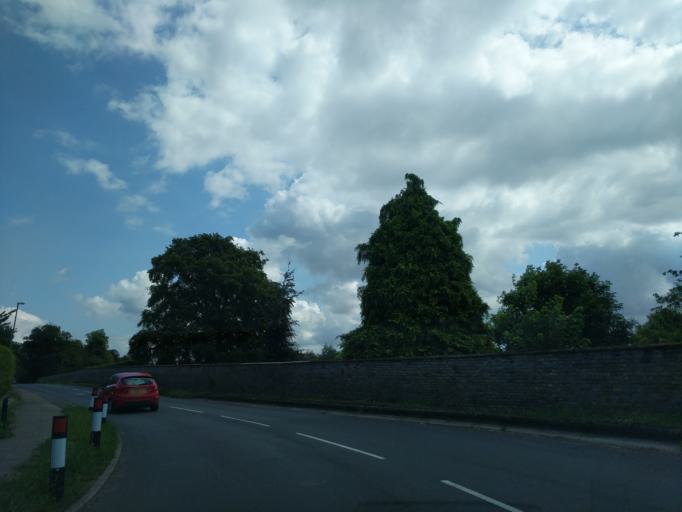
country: GB
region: England
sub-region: Cambridgeshire
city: Isleham
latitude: 52.2995
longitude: 0.4395
